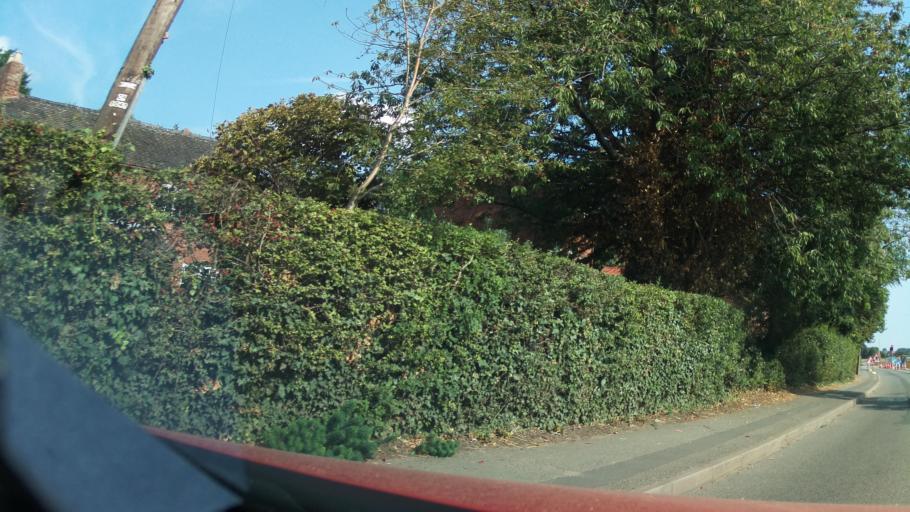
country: GB
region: England
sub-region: Staffordshire
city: Whittington
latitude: 52.6912
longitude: -1.7912
